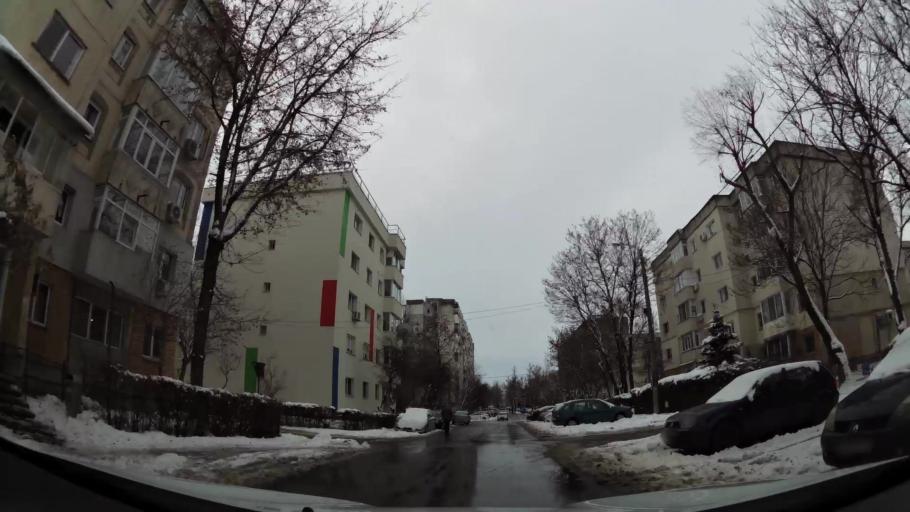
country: RO
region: Bucuresti
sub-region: Municipiul Bucuresti
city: Bucuresti
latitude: 44.3926
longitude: 26.1128
